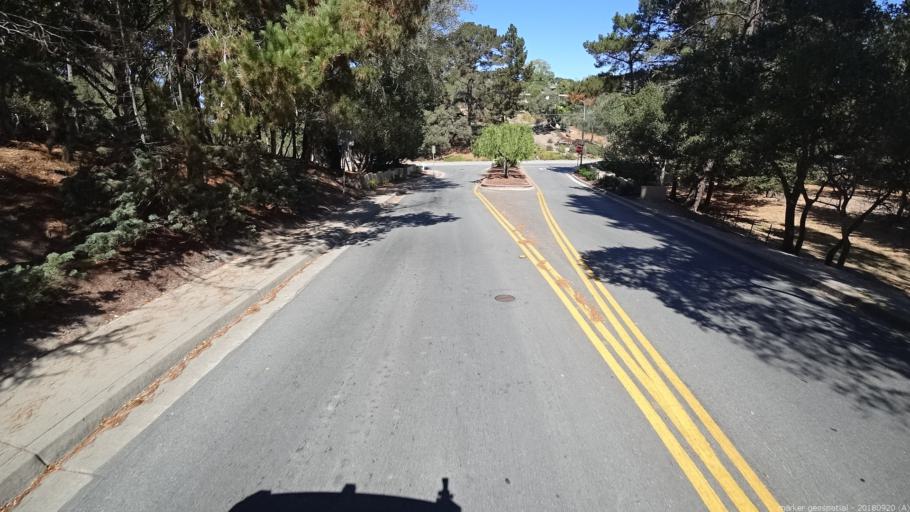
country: US
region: California
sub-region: Monterey County
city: Del Rey Oaks
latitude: 36.5812
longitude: -121.8627
